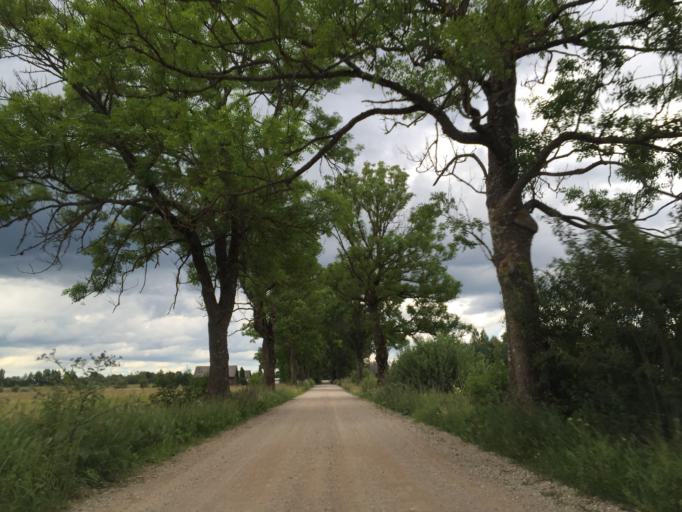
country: LV
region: Malpils
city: Malpils
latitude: 56.9207
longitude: 25.0044
